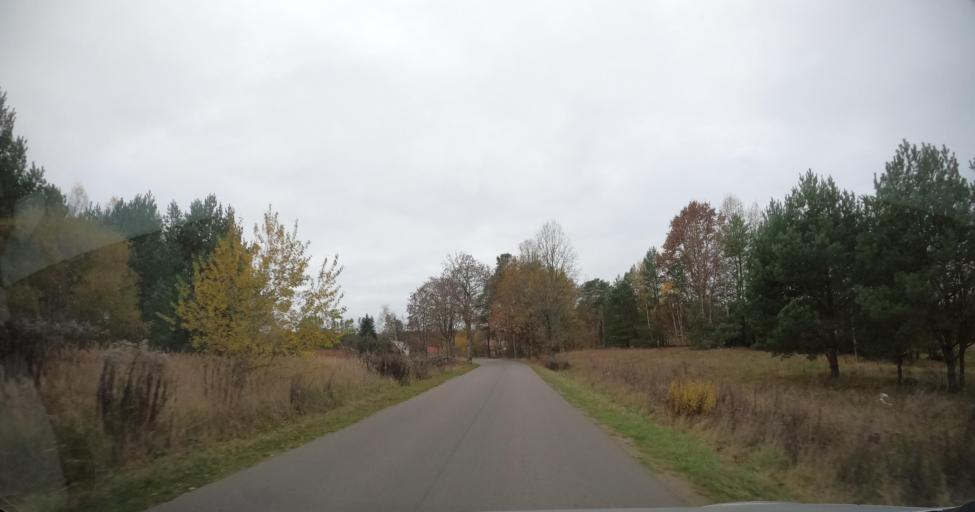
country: PL
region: West Pomeranian Voivodeship
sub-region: Powiat swidwinski
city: Polczyn-Zdroj
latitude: 53.7811
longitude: 16.1708
